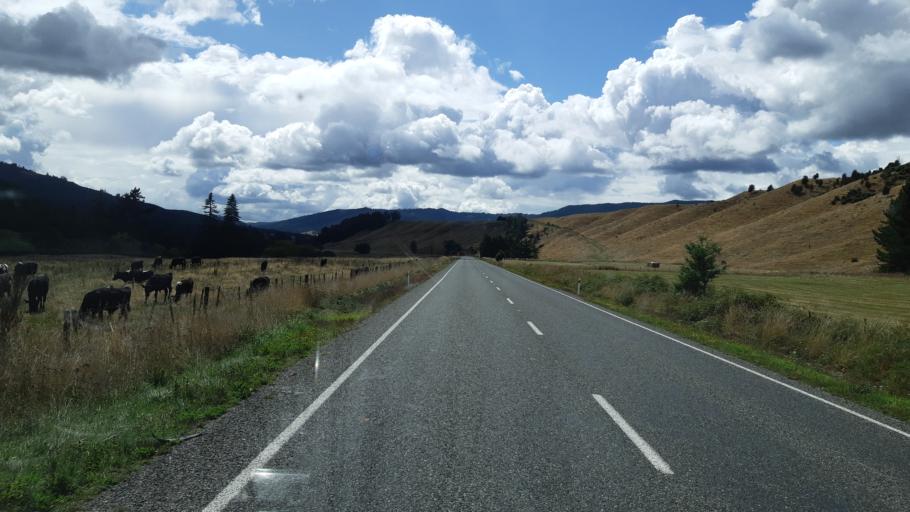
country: NZ
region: Tasman
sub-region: Tasman District
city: Wakefield
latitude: -41.5752
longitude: 172.7709
